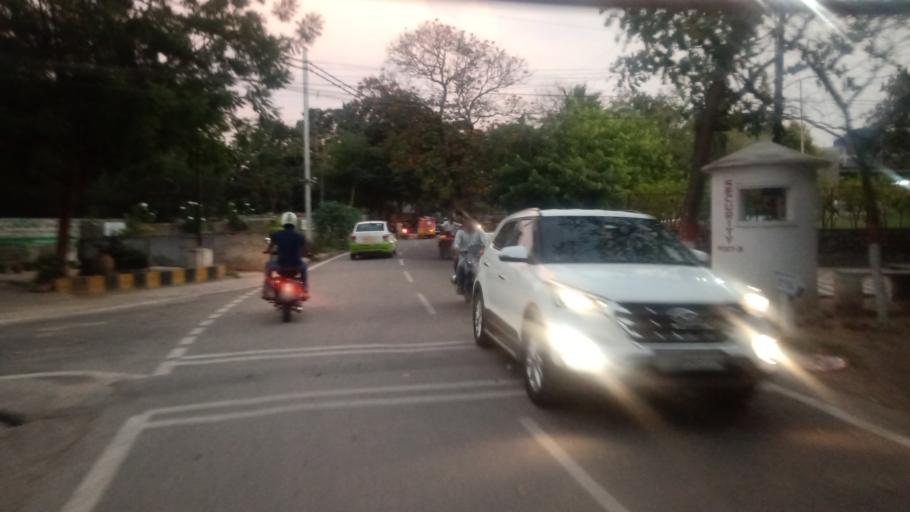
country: IN
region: Telangana
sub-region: Rangareddi
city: Kukatpalli
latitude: 17.5016
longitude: 78.3984
